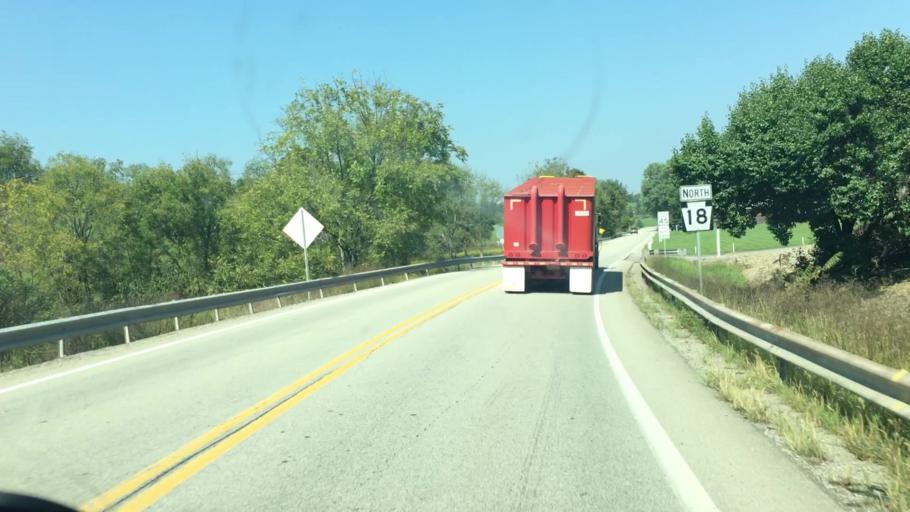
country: US
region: Pennsylvania
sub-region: Washington County
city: Washington
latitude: 40.1050
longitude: -80.2929
